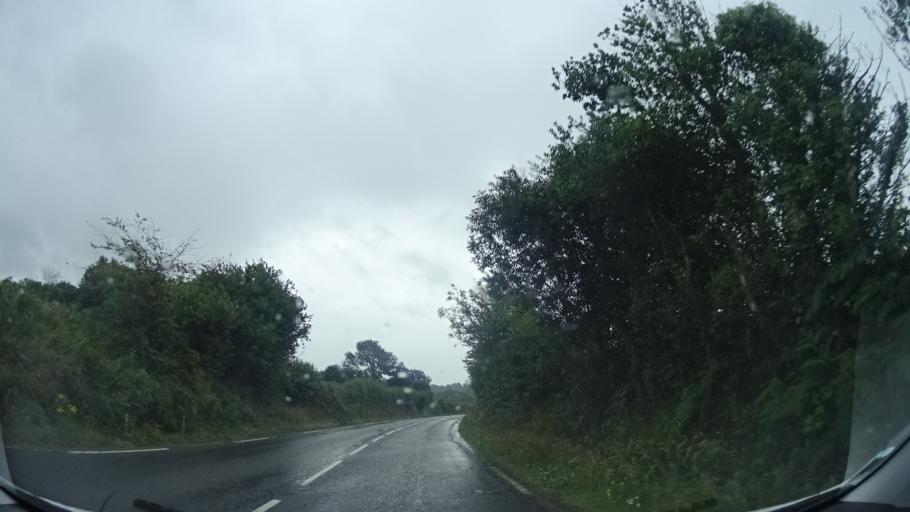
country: FR
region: Lower Normandy
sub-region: Departement de la Manche
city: Beaumont-Hague
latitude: 49.6057
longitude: -1.7866
